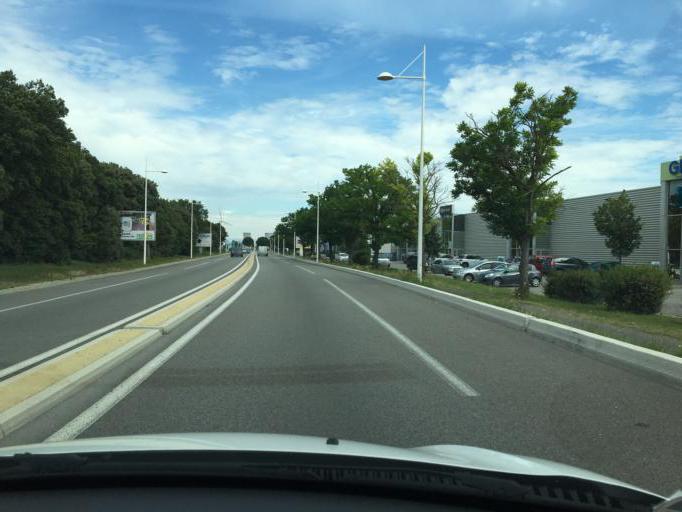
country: FR
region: Provence-Alpes-Cote d'Azur
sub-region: Departement du Vaucluse
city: Bollene
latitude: 44.2957
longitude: 4.7525
